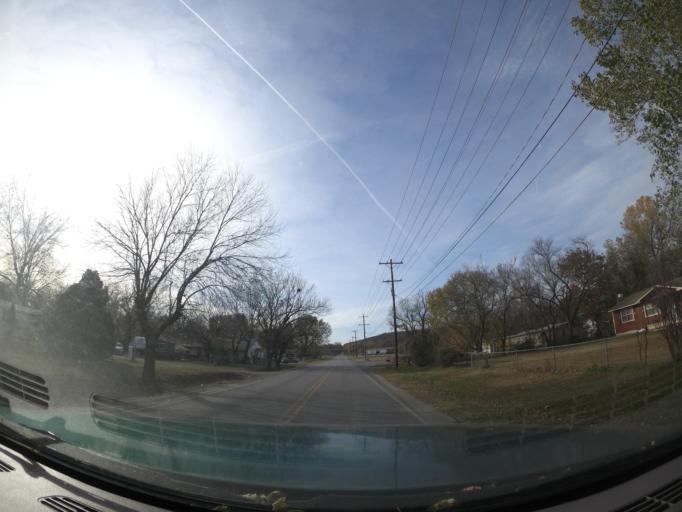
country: US
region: Oklahoma
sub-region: Tulsa County
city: Turley
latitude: 36.2496
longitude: -95.9720
